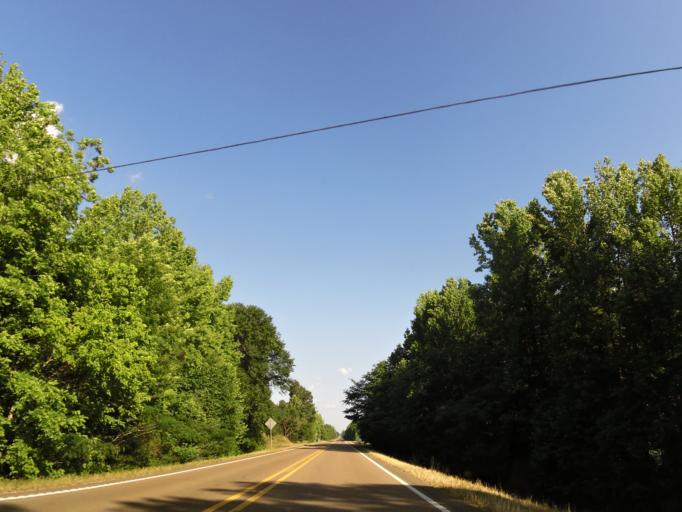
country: US
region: Mississippi
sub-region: Yalobusha County
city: Water Valley
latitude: 34.1757
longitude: -89.4558
